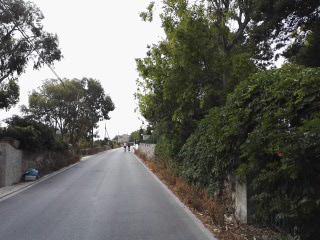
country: IT
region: Sicily
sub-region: Trapani
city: Favignana
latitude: 37.9264
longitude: 12.3346
